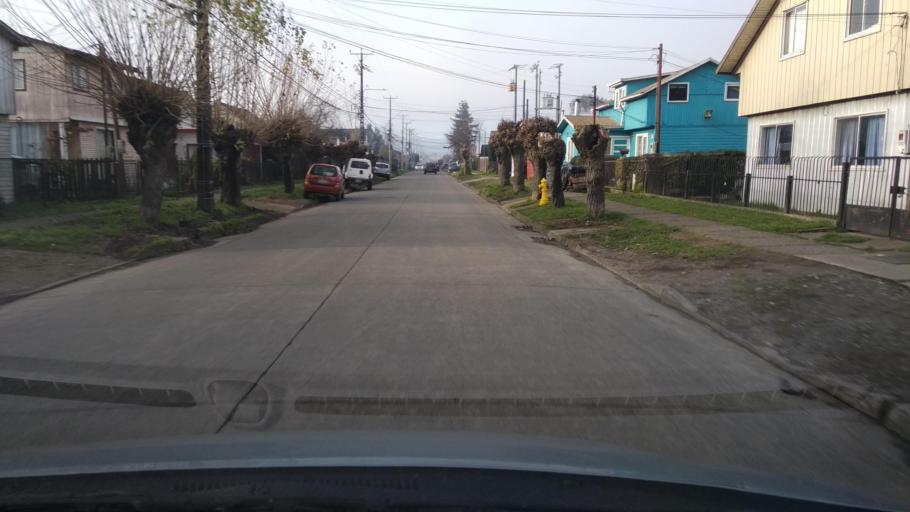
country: CL
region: Los Lagos
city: Las Animas
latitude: -39.8116
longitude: -73.2289
